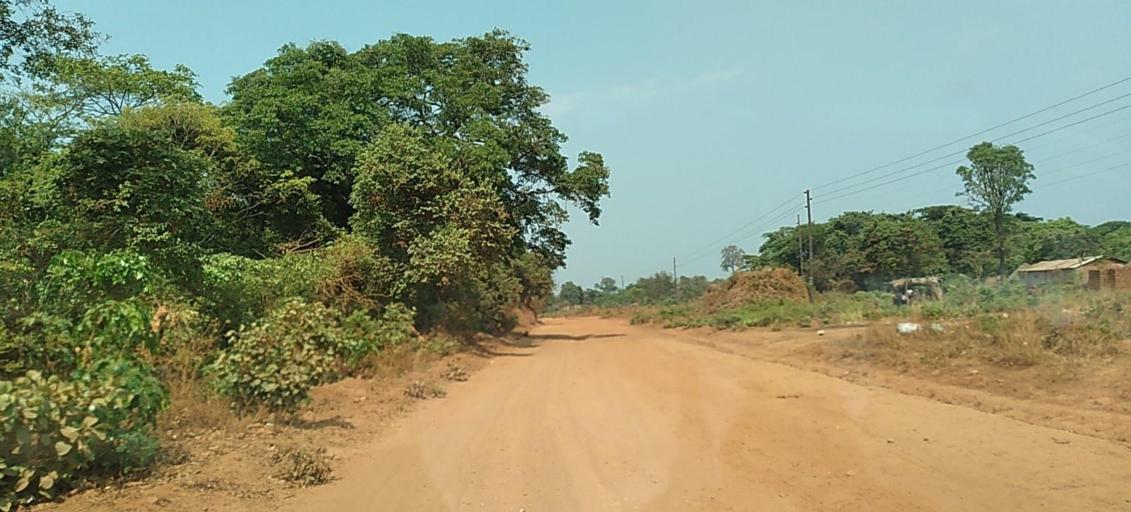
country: ZM
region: Copperbelt
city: Chingola
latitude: -13.0445
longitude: 27.4372
